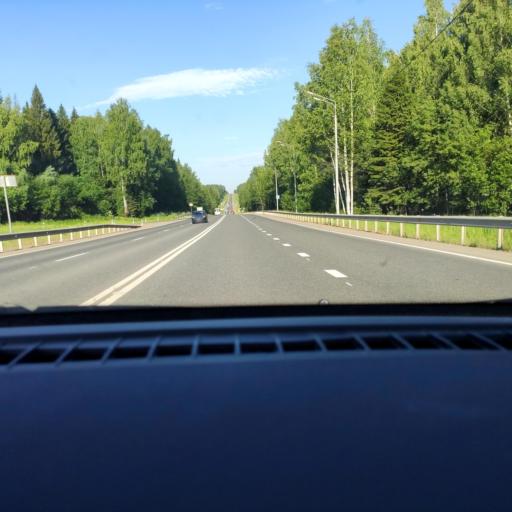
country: RU
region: Udmurtiya
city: Khokhryaki
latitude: 56.9168
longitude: 53.4502
